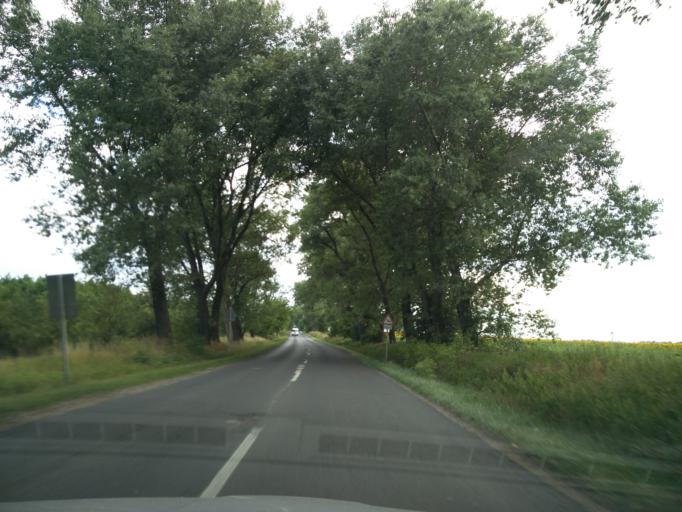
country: HU
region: Fejer
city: Szarliget
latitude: 47.4589
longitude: 18.5563
